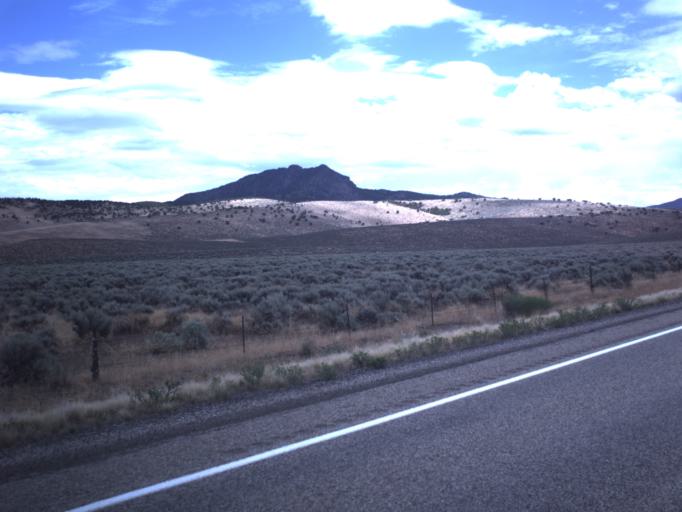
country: US
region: Utah
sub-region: Beaver County
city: Beaver
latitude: 38.0691
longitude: -112.6814
